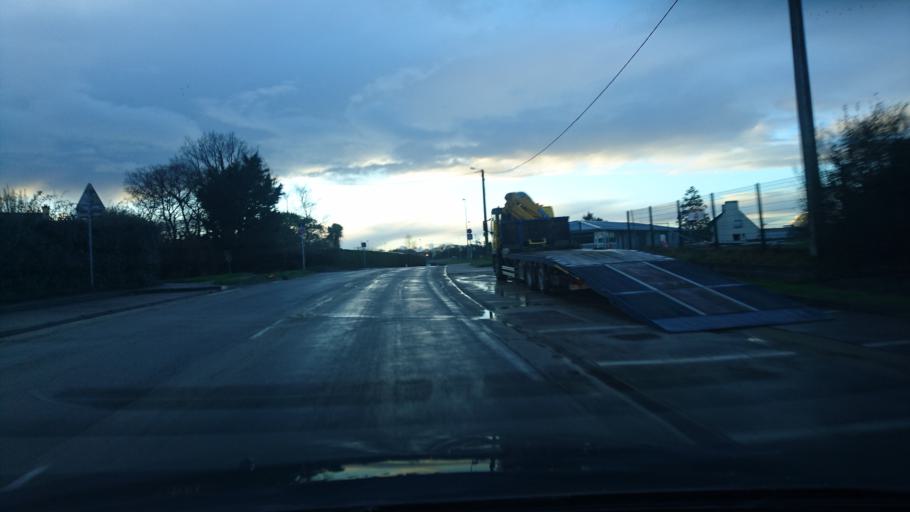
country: FR
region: Brittany
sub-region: Departement du Finistere
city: Guilers
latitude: 48.4248
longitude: -4.5673
